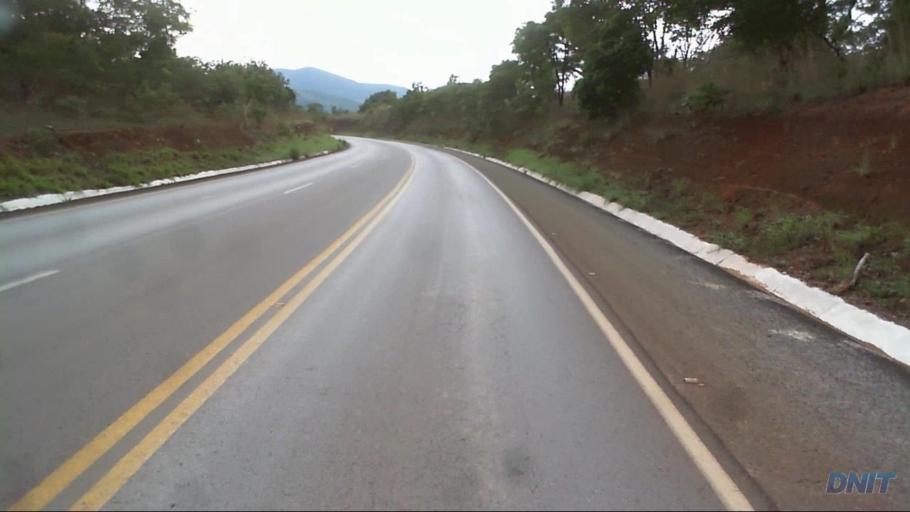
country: BR
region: Goias
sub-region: Barro Alto
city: Barro Alto
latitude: -14.8664
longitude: -49.0154
